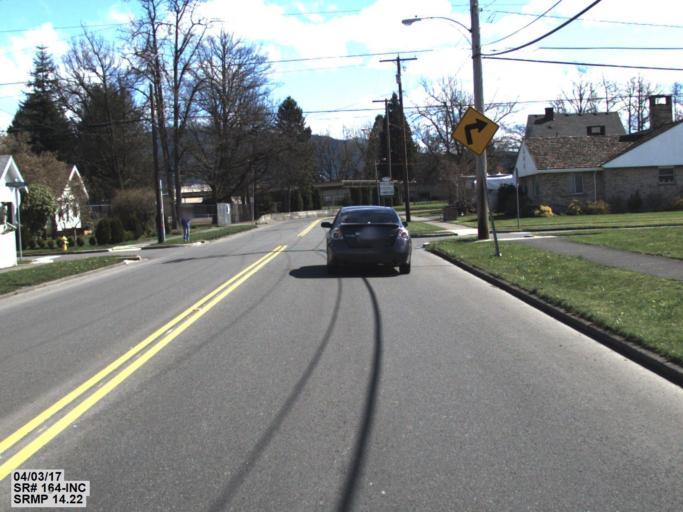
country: US
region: Washington
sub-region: King County
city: Enumclaw
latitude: 47.2066
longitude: -121.9966
